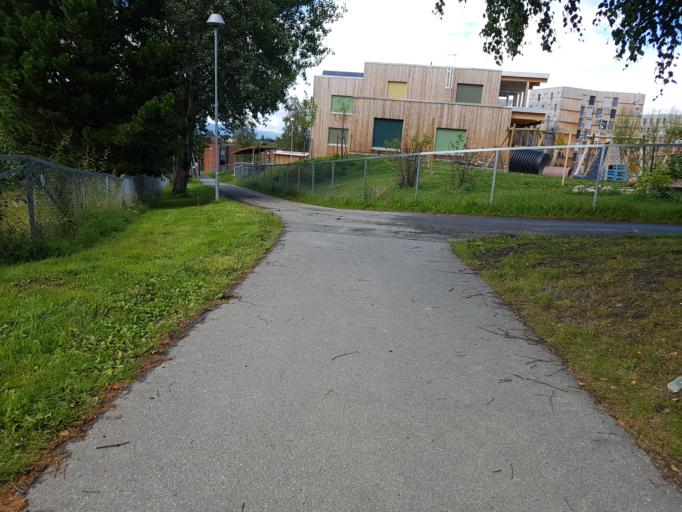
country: NO
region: Sor-Trondelag
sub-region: Trondheim
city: Trondheim
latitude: 63.4095
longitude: 10.4310
